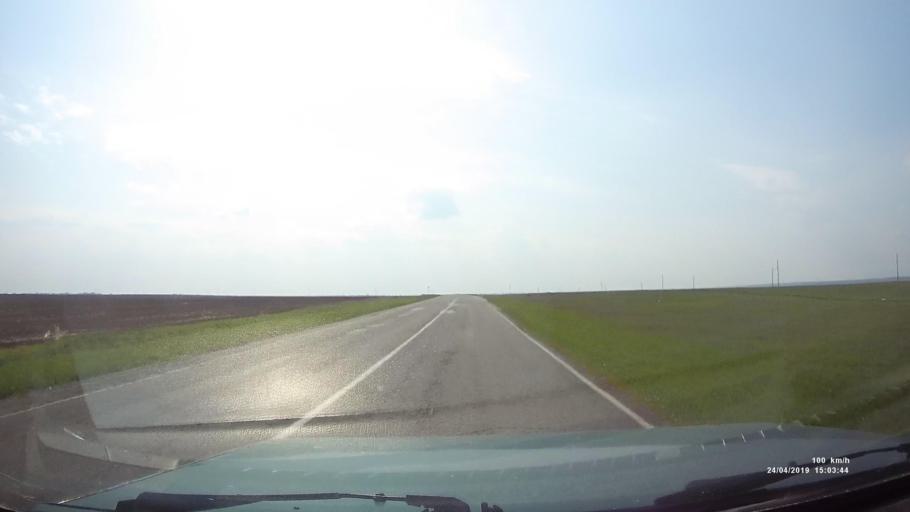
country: RU
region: Rostov
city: Remontnoye
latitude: 46.5642
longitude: 43.4856
